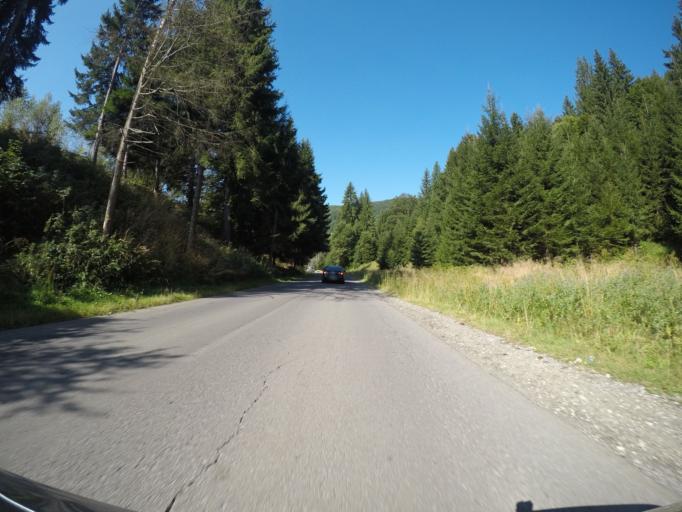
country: RO
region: Brasov
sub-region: Comuna Cristian
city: Cristian
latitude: 45.5933
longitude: 25.5295
